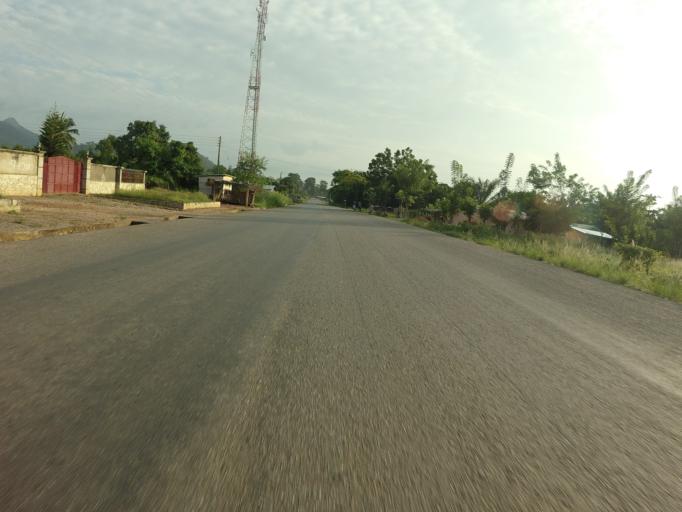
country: GH
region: Volta
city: Kpandu
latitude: 6.9027
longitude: 0.4371
